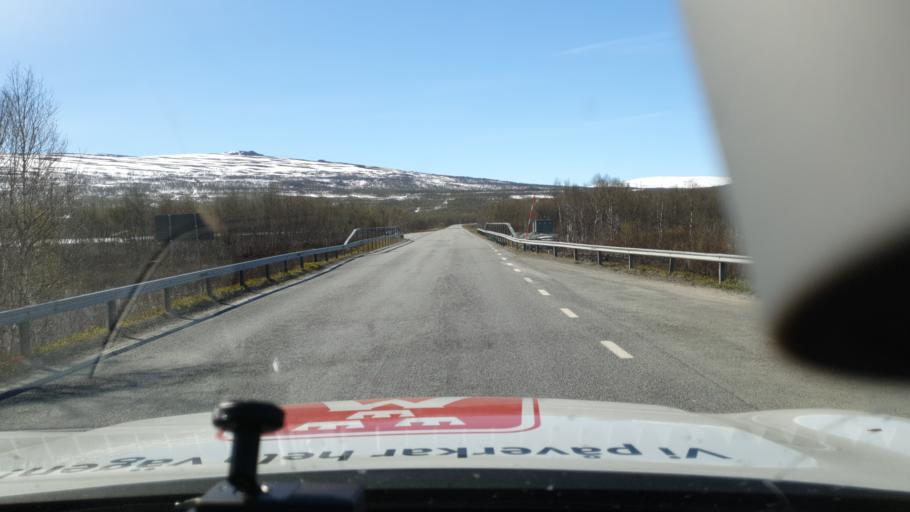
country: NO
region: Nordland
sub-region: Hattfjelldal
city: Hattfjelldal
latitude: 65.7228
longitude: 14.6114
